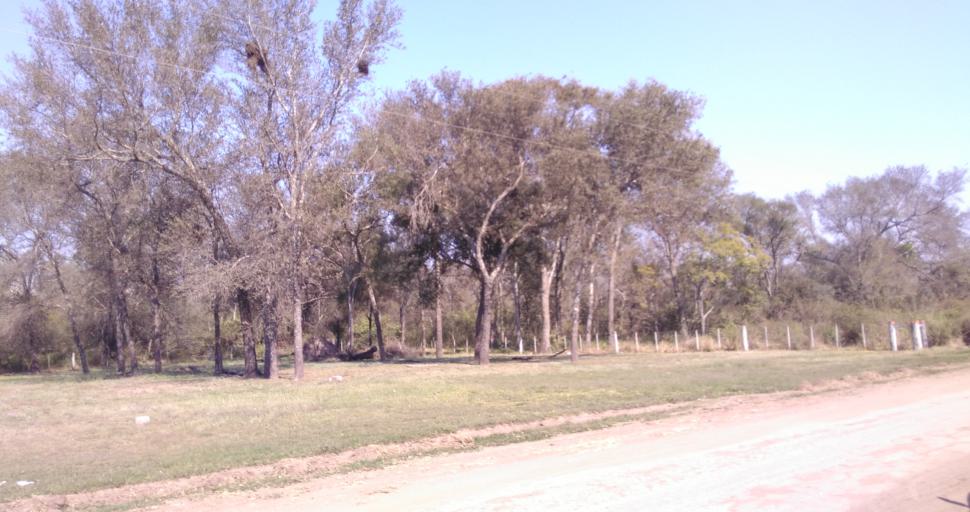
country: AR
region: Chaco
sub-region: Departamento de Quitilipi
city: Quitilipi
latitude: -26.6759
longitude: -60.1980
